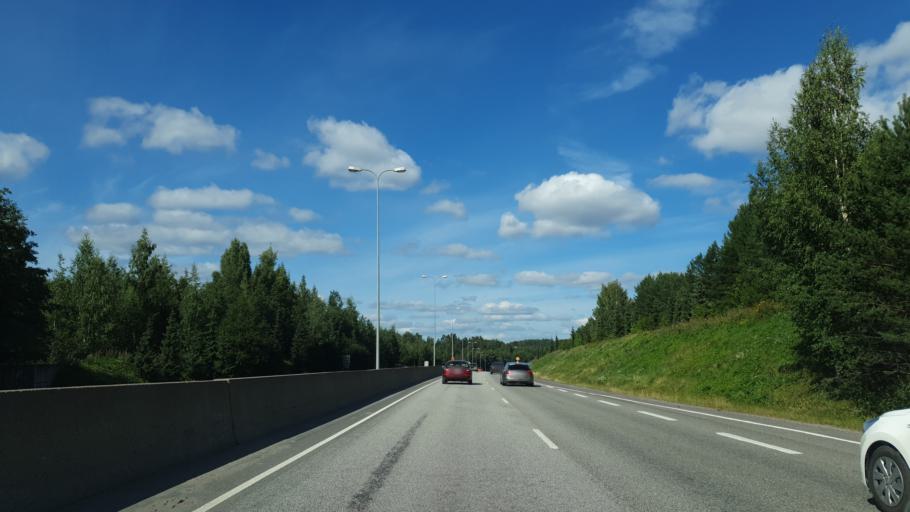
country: FI
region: Central Finland
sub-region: Jyvaeskylae
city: Jyvaeskylae
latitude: 62.2211
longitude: 25.7251
